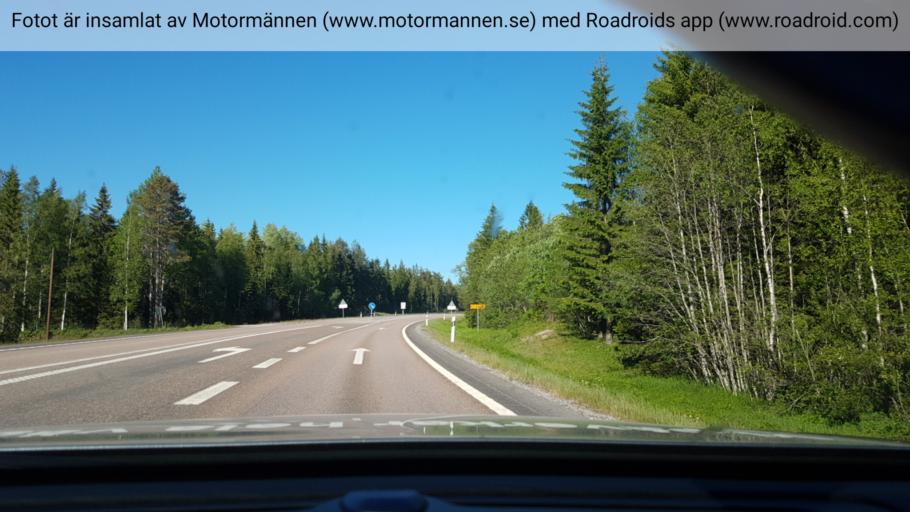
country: SE
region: Vaesternorrland
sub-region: Timra Kommun
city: Soraker
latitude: 62.5568
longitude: 17.6447
